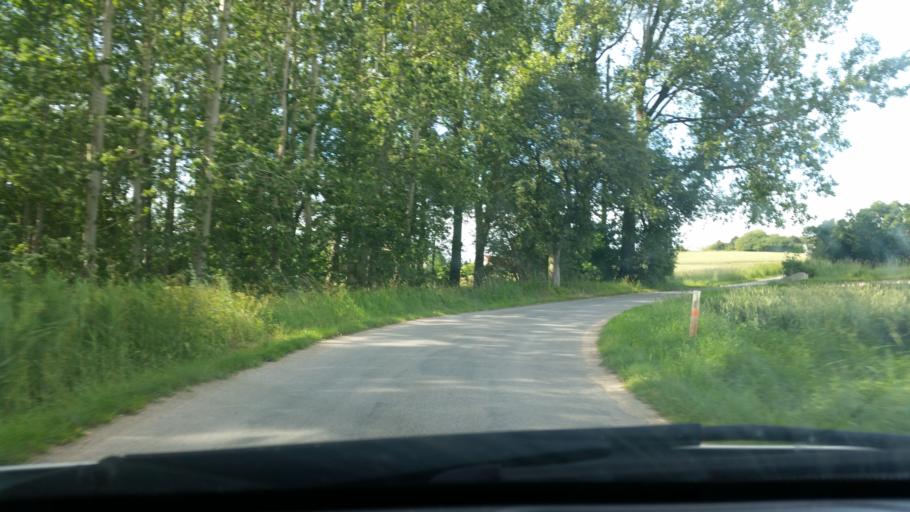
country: DK
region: Central Jutland
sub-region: Samso Kommune
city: Tranebjerg
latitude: 55.7817
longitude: 10.5527
